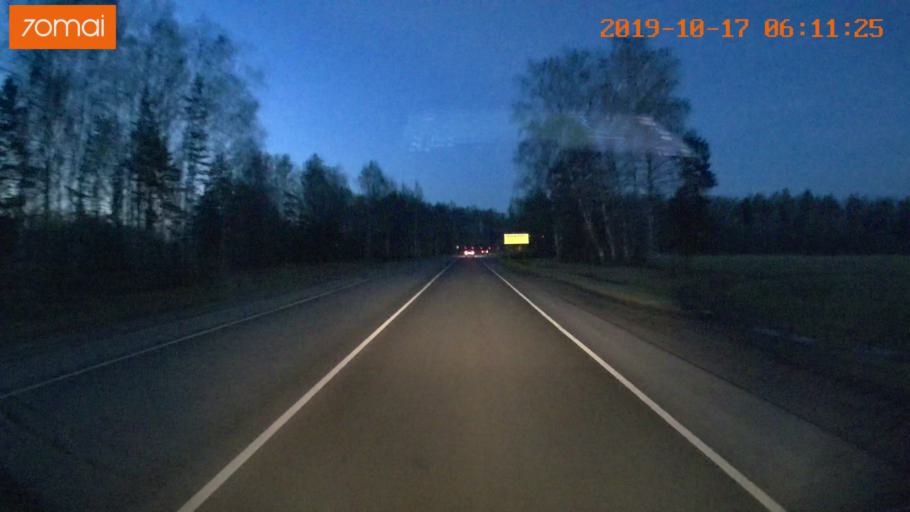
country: RU
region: Ivanovo
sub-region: Gorod Ivanovo
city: Ivanovo
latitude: 56.9195
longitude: 40.9581
